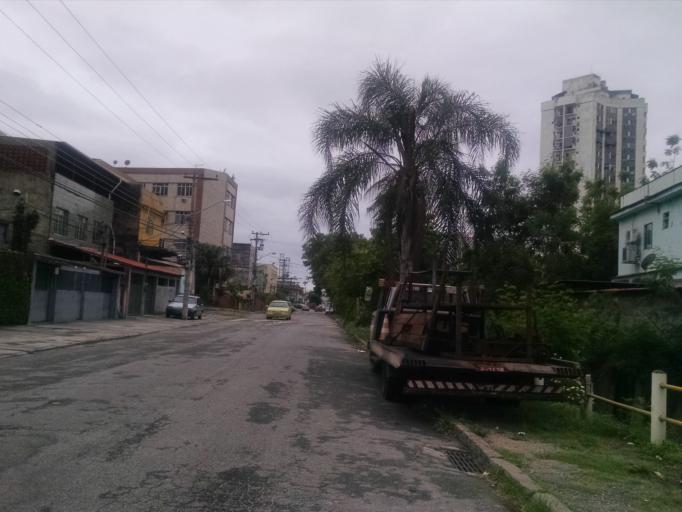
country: BR
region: Rio de Janeiro
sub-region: Duque De Caxias
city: Duque de Caxias
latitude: -22.8349
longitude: -43.3102
